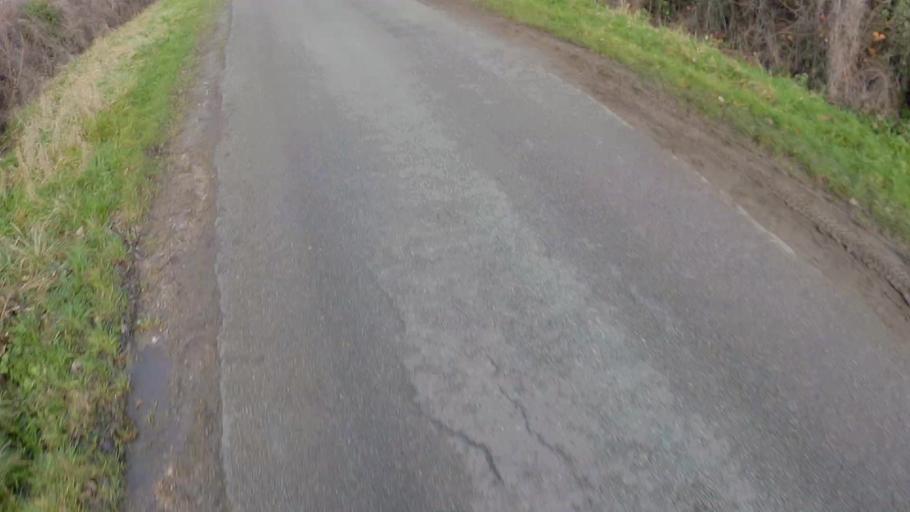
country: GB
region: England
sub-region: Lincolnshire
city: Bourne
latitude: 52.7498
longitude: -0.4166
